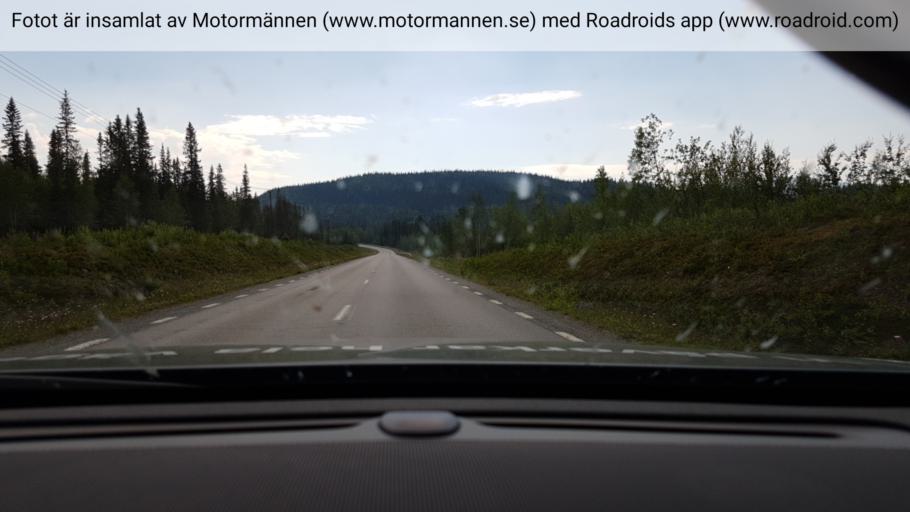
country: SE
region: Vaesterbotten
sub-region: Vilhelmina Kommun
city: Sjoberg
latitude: 65.5121
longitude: 15.6476
